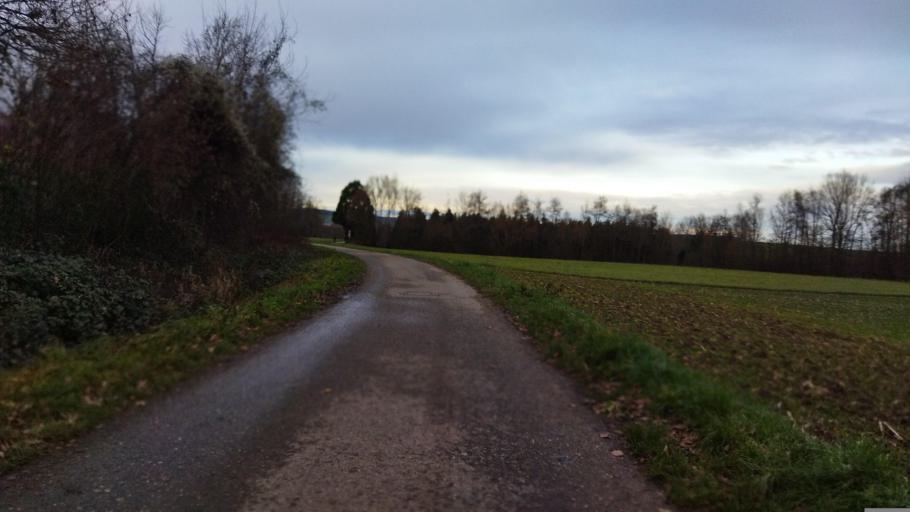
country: DE
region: Baden-Wuerttemberg
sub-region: Regierungsbezirk Stuttgart
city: Guglingen
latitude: 49.0523
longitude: 9.0036
